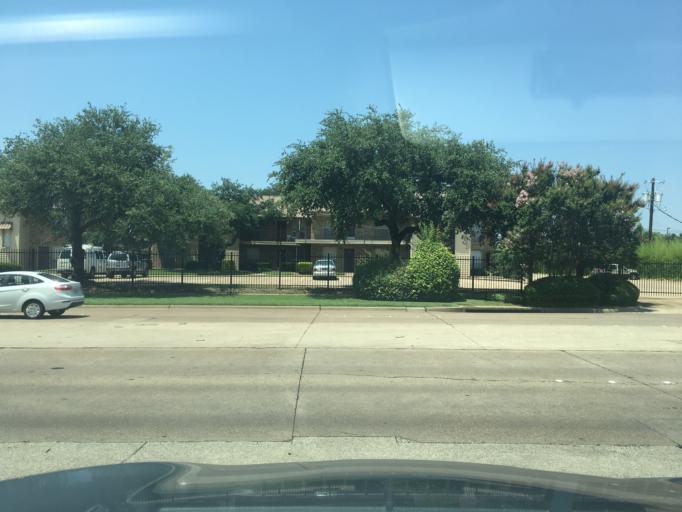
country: US
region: Texas
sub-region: Dallas County
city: Richardson
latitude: 32.9165
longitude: -96.7032
